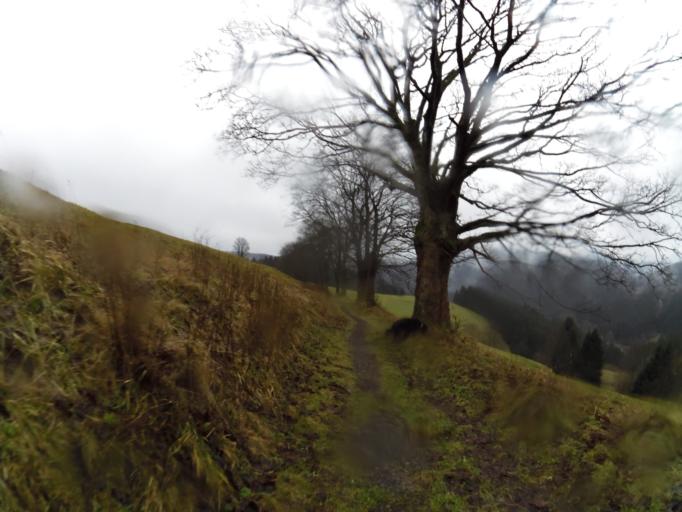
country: DE
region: Lower Saxony
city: Sankt Andreasberg
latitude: 51.7055
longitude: 10.5090
